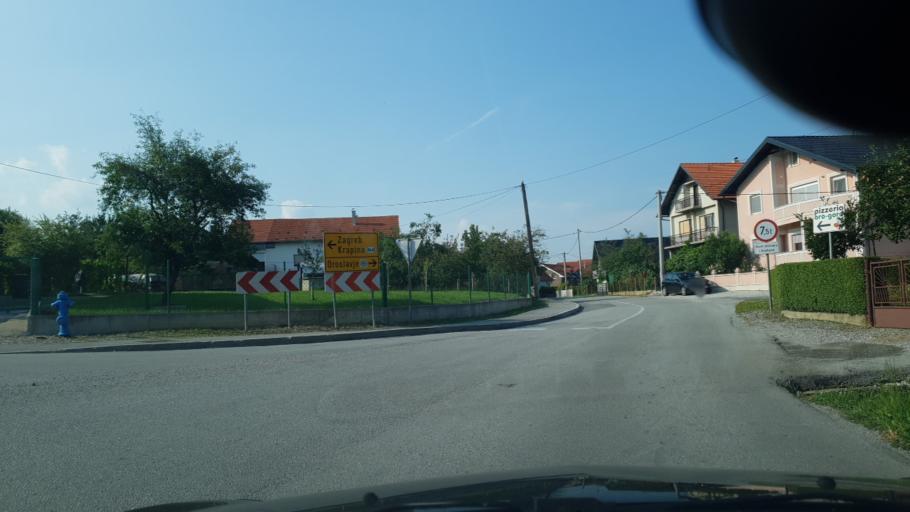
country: HR
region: Krapinsko-Zagorska
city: Oroslavje
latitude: 45.9782
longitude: 15.9211
